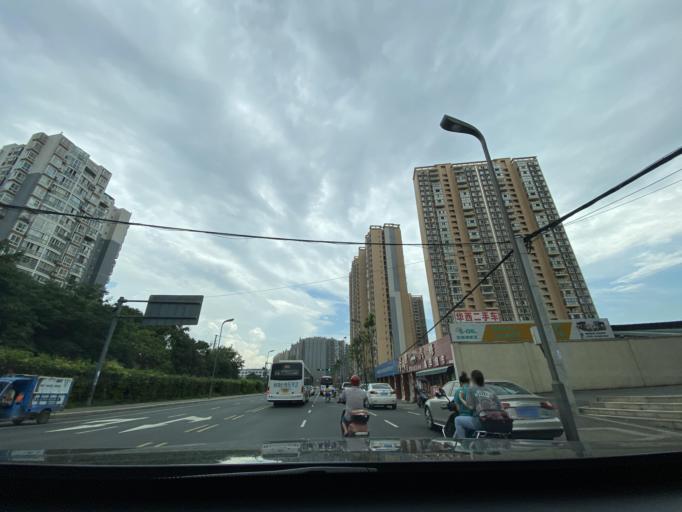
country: CN
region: Sichuan
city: Dongsheng
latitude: 30.5132
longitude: 104.0392
